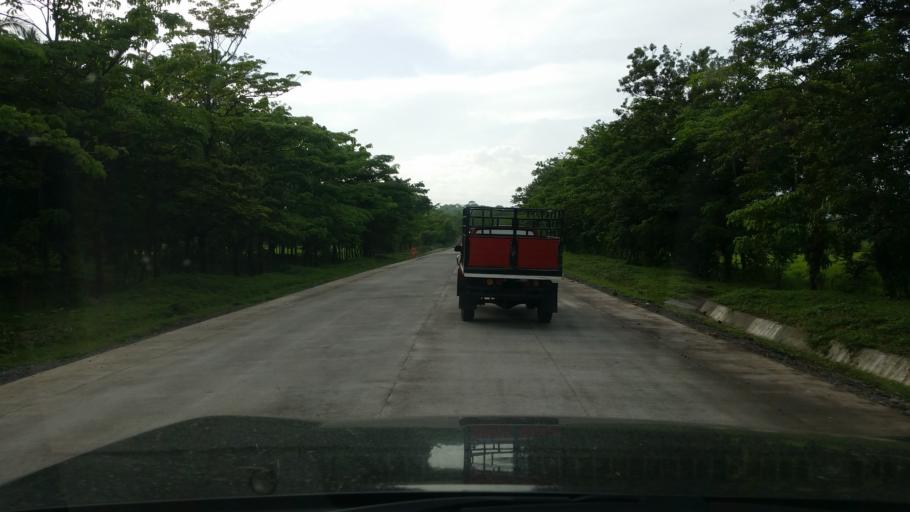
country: NI
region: Matagalpa
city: Rio Blanco
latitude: 13.0969
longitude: -85.0640
